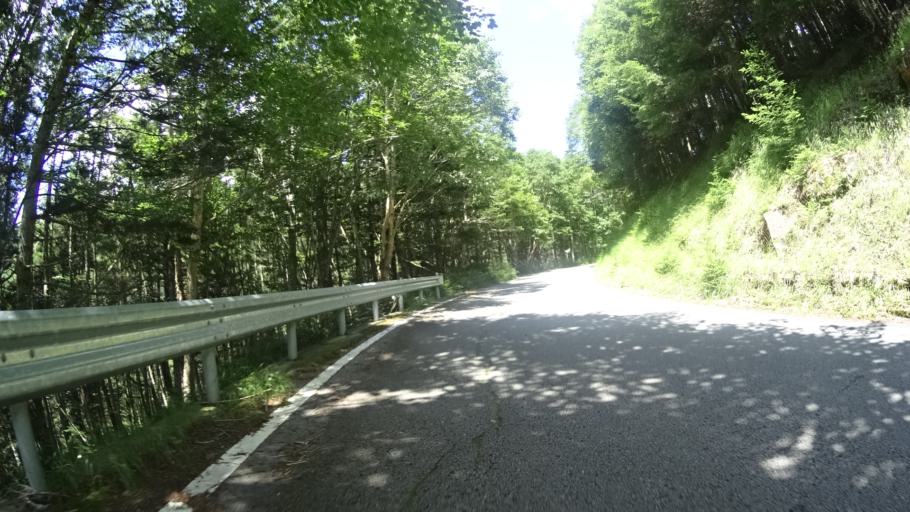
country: JP
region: Yamanashi
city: Enzan
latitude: 35.8577
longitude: 138.6453
